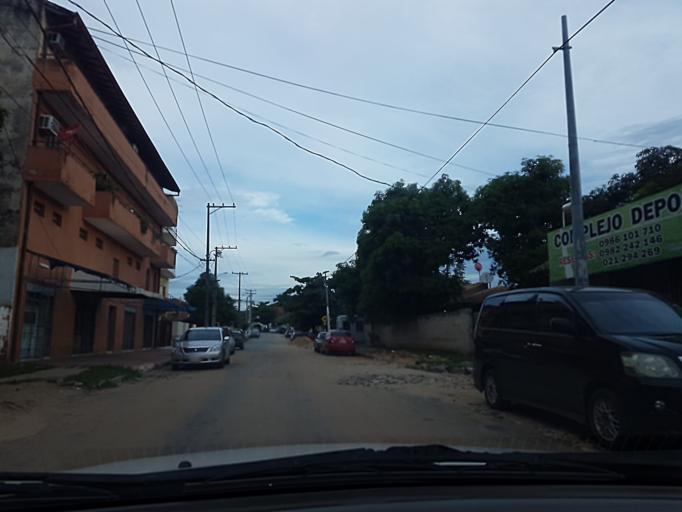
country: PY
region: Asuncion
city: Asuncion
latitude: -25.2543
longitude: -57.5793
